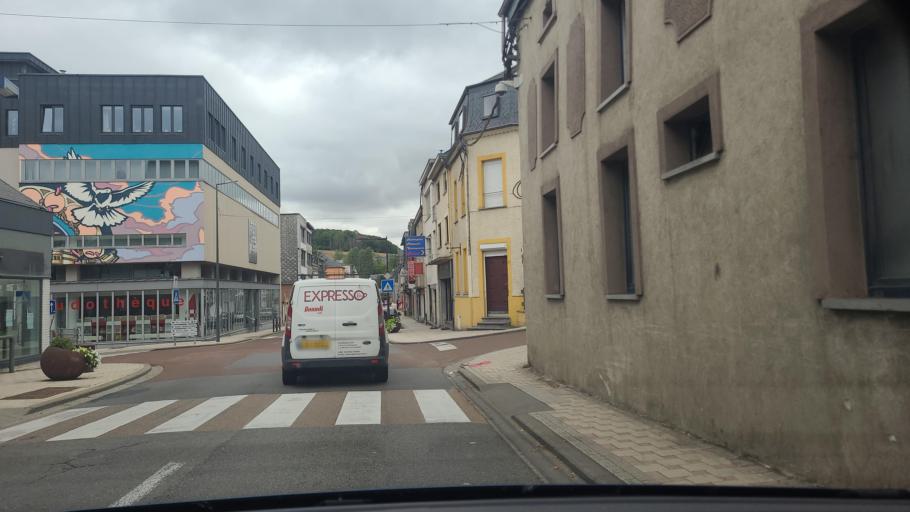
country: LU
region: Luxembourg
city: Rodange
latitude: 49.5630
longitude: 5.8329
